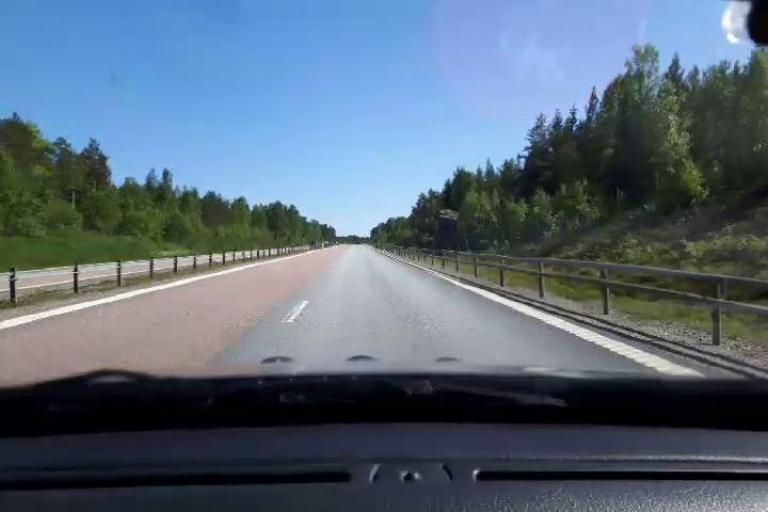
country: SE
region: Gaevleborg
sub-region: Soderhamns Kommun
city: Soderhamn
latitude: 61.3281
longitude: 17.0244
